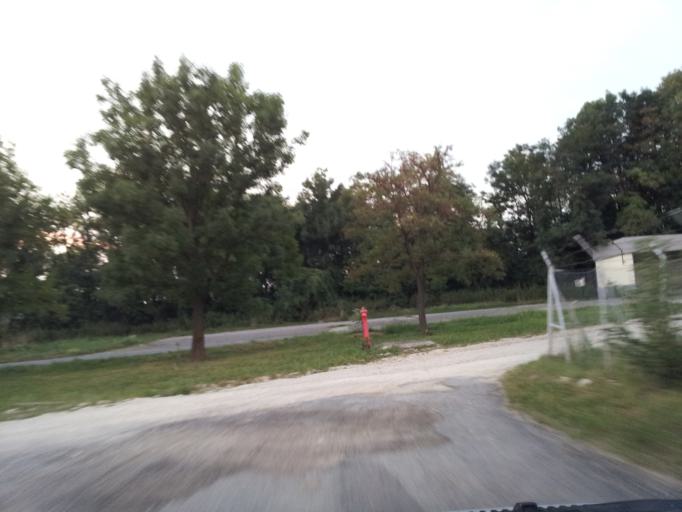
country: HU
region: Veszprem
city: Zirc
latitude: 47.2727
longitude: 17.8767
